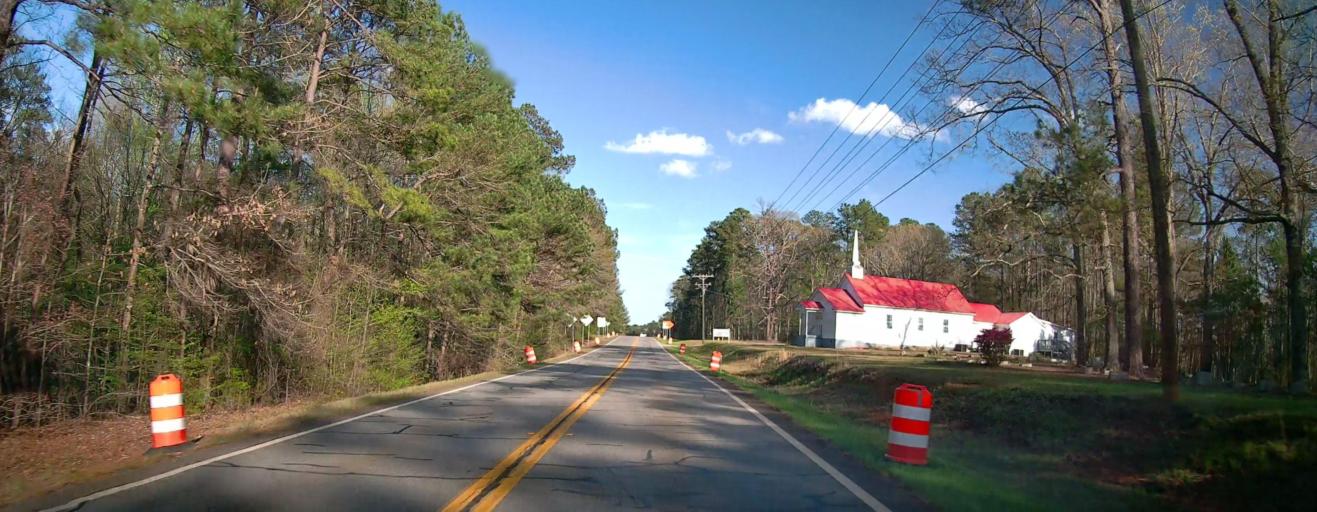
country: US
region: Georgia
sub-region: Baldwin County
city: Milledgeville
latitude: 33.1603
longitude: -83.3680
